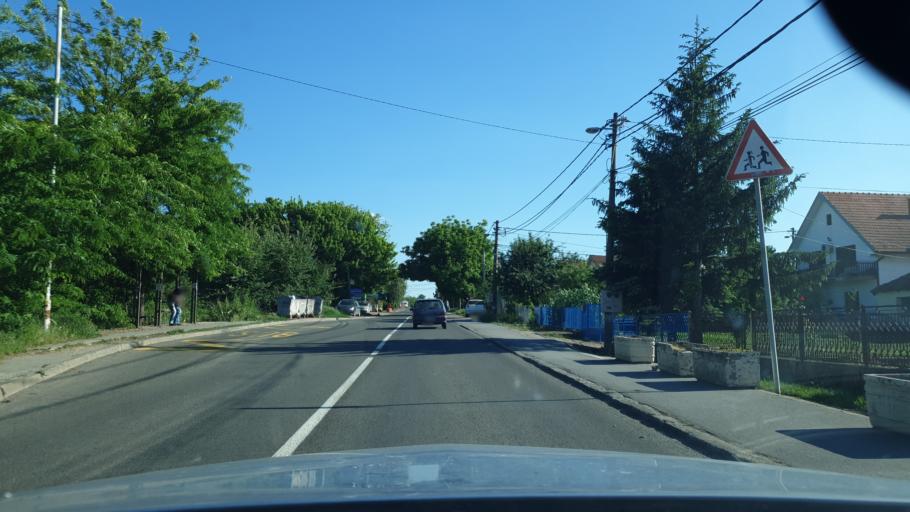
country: RS
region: Central Serbia
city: Sremcica
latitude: 44.7143
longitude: 20.3682
